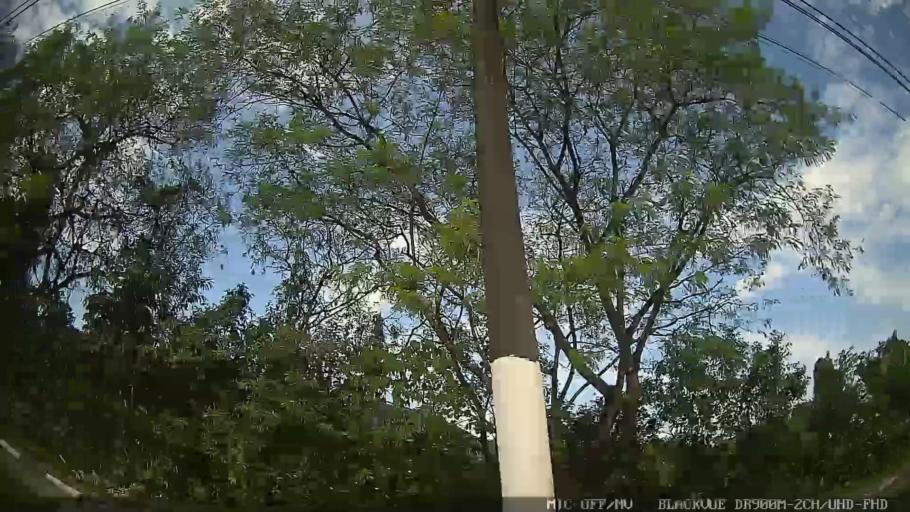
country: BR
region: Sao Paulo
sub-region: Guaruja
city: Guaruja
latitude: -23.9670
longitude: -46.2636
